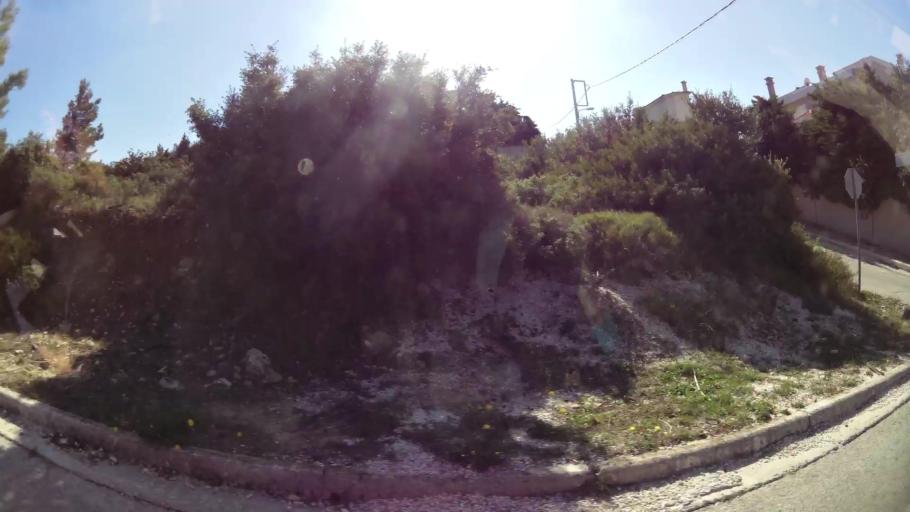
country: GR
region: Attica
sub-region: Nomarchia Anatolikis Attikis
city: Dhrafi
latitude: 38.0187
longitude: 23.9133
